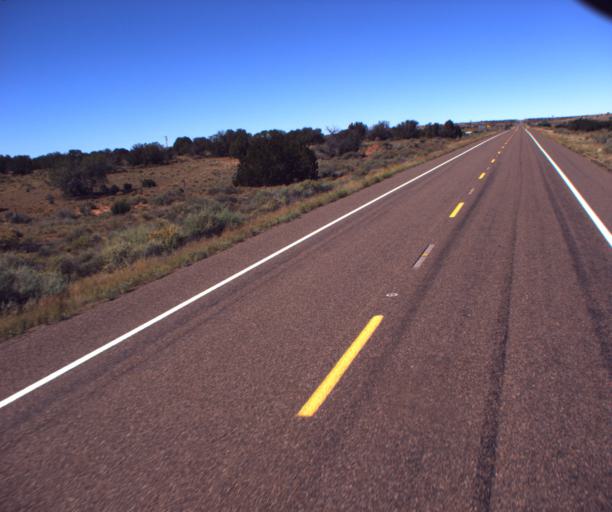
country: US
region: Arizona
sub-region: Apache County
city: Saint Johns
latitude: 34.6176
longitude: -109.6586
